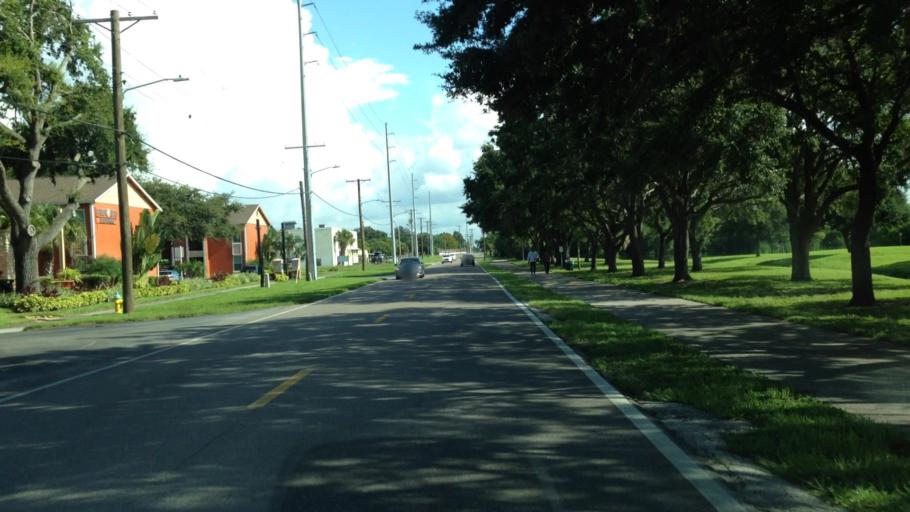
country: US
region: Florida
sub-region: Hillsborough County
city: Tampa
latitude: 27.8763
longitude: -82.5186
